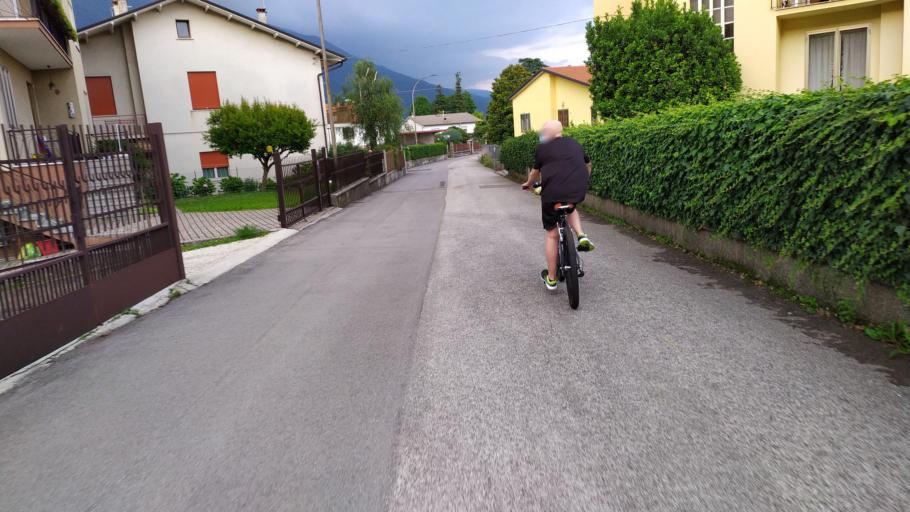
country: IT
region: Veneto
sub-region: Provincia di Vicenza
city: Piovene Rocchette
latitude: 45.7610
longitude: 11.4346
